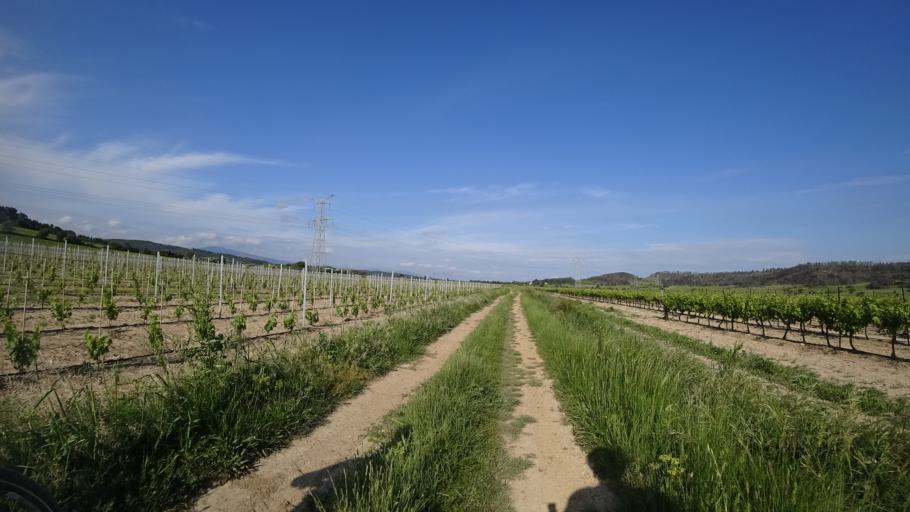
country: FR
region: Languedoc-Roussillon
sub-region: Departement de l'Herault
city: Olonzac
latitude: 43.2378
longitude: 2.7209
